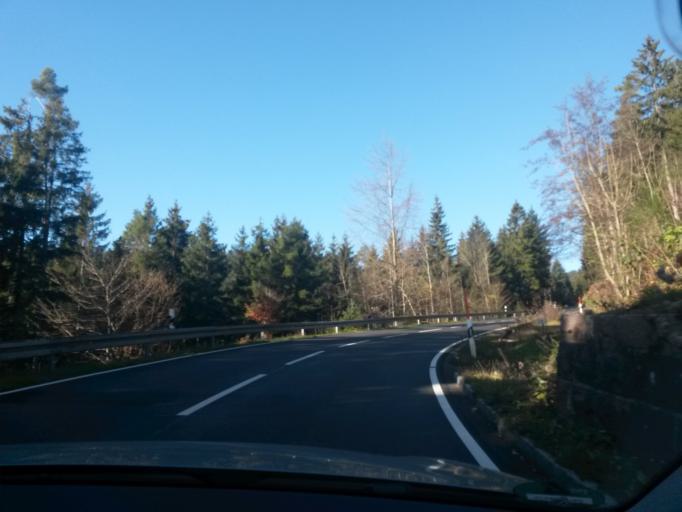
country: DE
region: Baden-Wuerttemberg
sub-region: Karlsruhe Region
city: Bad Rippoldsau-Schapbach
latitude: 48.4501
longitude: 8.2913
